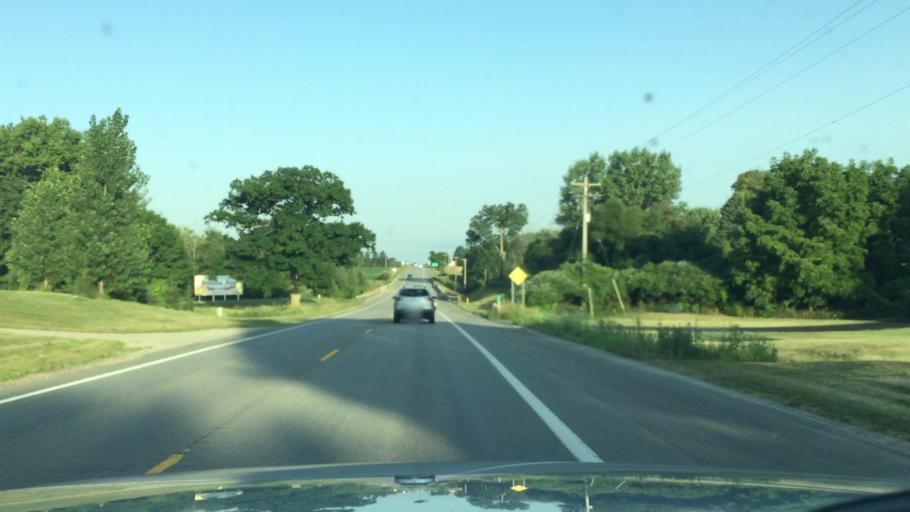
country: US
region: Michigan
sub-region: Gratiot County
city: Ithaca
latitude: 43.1761
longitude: -84.6701
